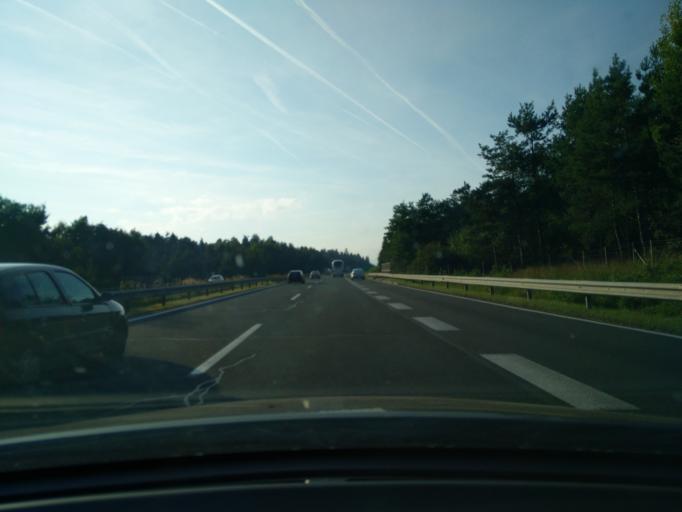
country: SI
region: Kranj
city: Mlaka pri Kranju
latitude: 46.2665
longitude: 14.3386
